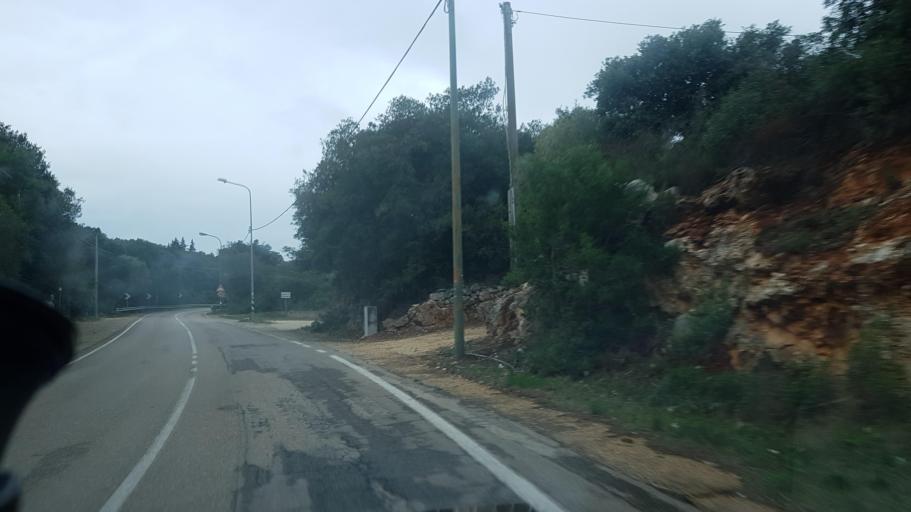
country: IT
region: Apulia
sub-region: Provincia di Brindisi
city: Ostuni
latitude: 40.7332
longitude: 17.5559
